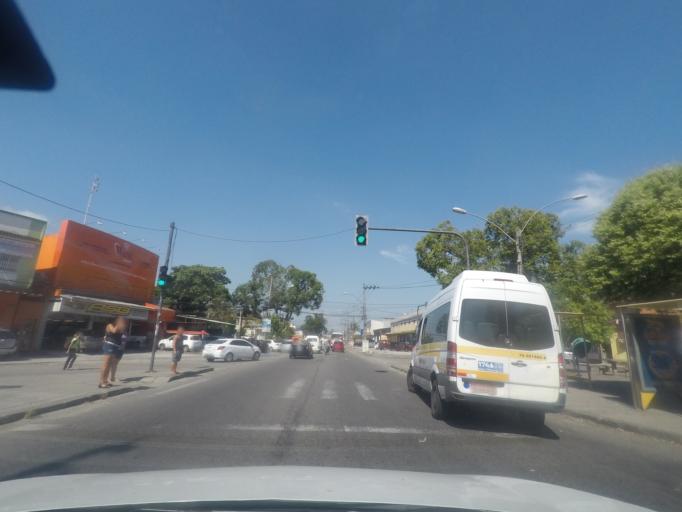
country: BR
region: Rio de Janeiro
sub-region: Nilopolis
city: Nilopolis
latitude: -22.8781
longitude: -43.4482
